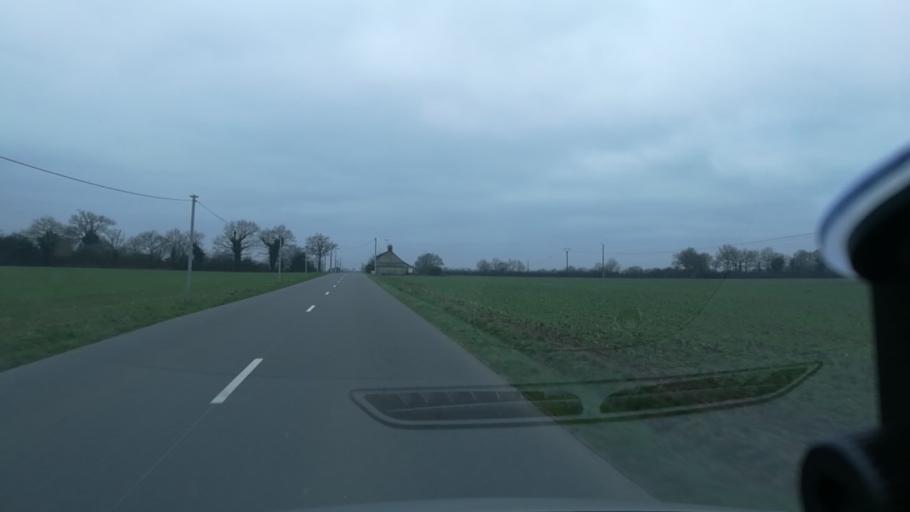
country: FR
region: Brittany
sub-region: Departement d'Ille-et-Vilaine
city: Coesmes
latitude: 47.8838
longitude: -1.4848
